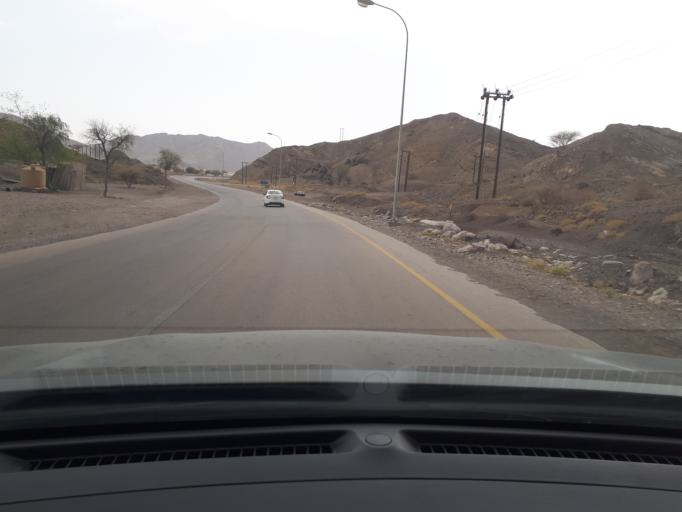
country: OM
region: Ash Sharqiyah
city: Badiyah
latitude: 22.5516
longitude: 59.0017
